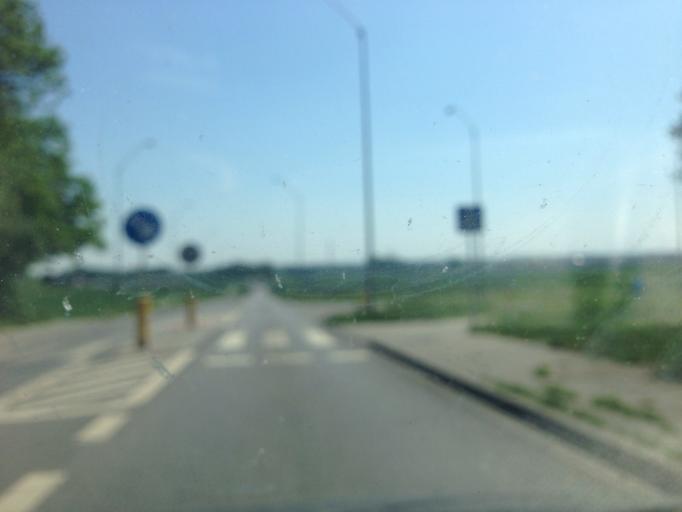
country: PL
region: Pomeranian Voivodeship
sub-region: Powiat tczewski
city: Pelplin
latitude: 53.9266
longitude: 18.6652
